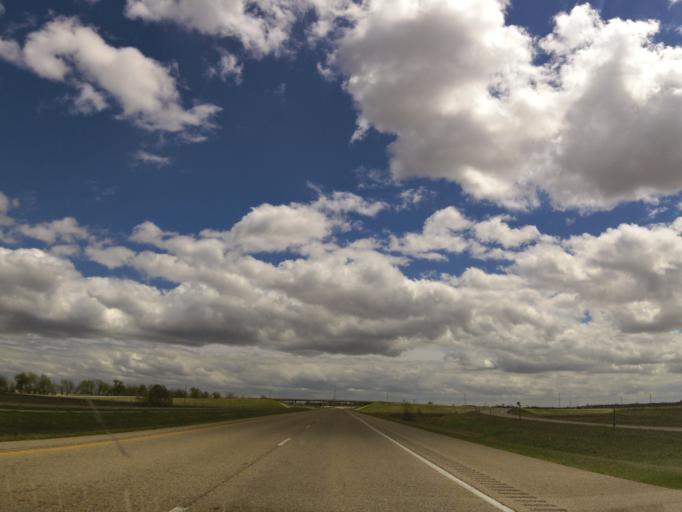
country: US
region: Arkansas
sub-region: Poinsett County
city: Marked Tree
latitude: 35.4755
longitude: -90.3395
